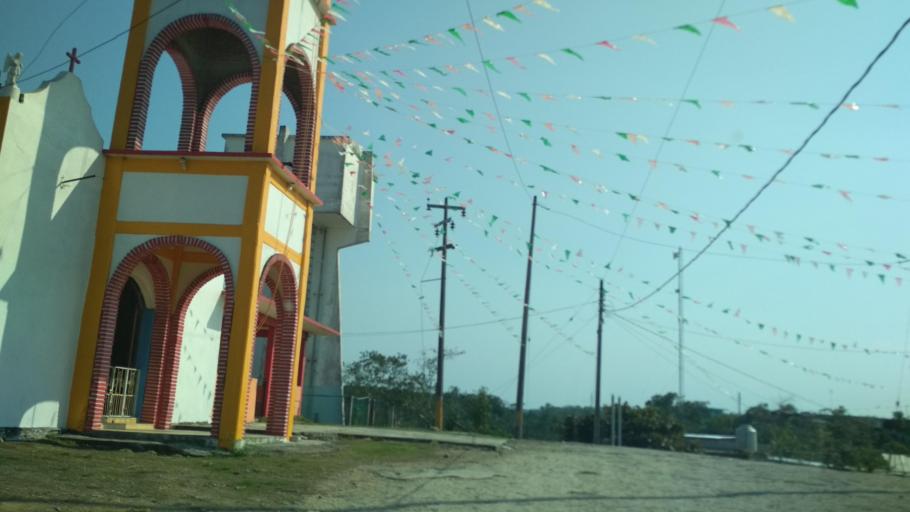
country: MX
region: Veracruz
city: Agua Dulce
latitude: 20.3880
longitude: -97.2130
